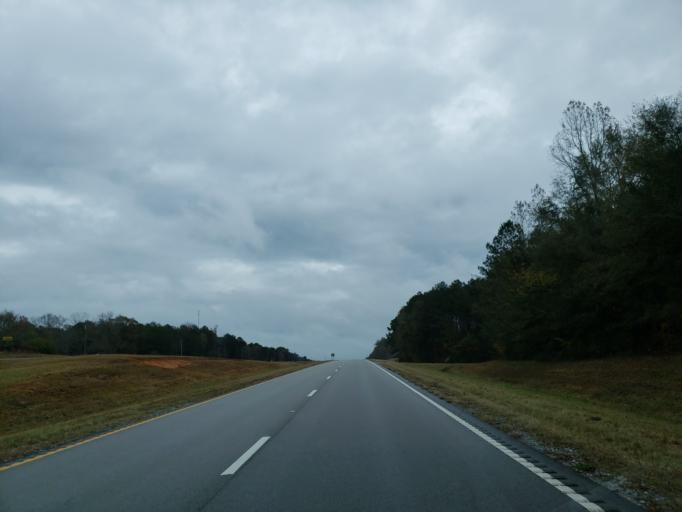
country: US
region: Mississippi
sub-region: Wayne County
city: Waynesboro
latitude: 31.6952
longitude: -88.7506
